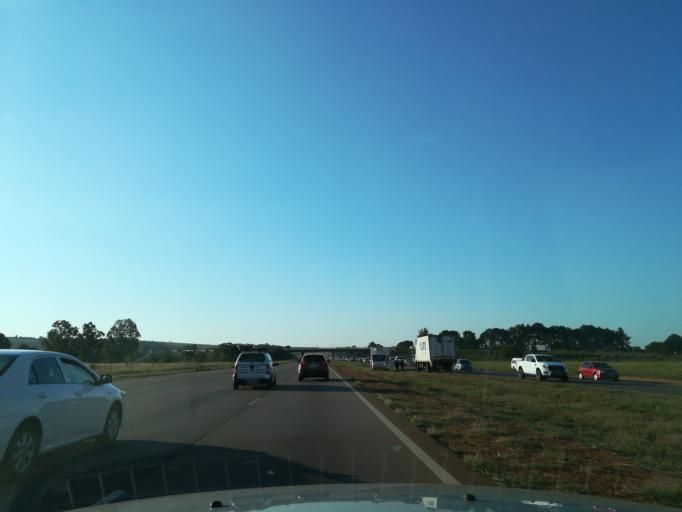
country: ZA
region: Gauteng
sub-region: City of Tshwane Metropolitan Municipality
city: Centurion
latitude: -25.8139
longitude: 28.1816
